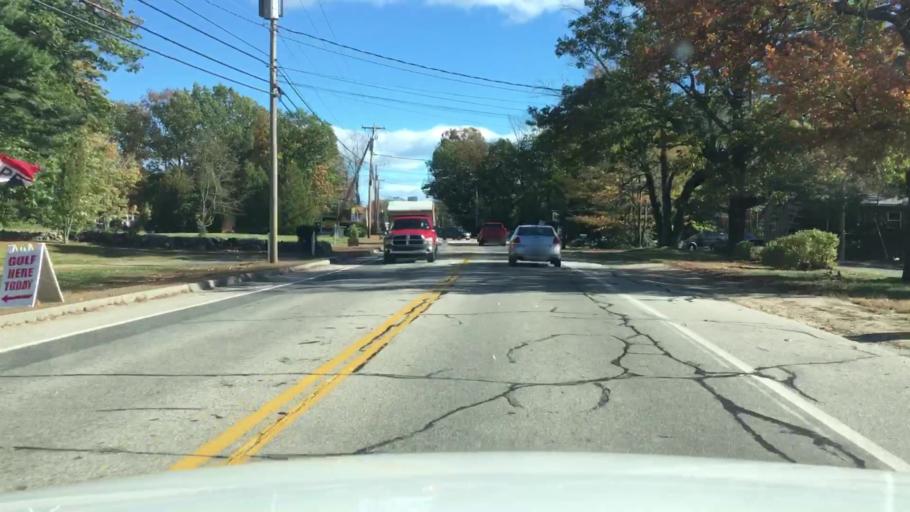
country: US
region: Maine
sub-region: York County
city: South Sanford
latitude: 43.4087
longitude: -70.7382
